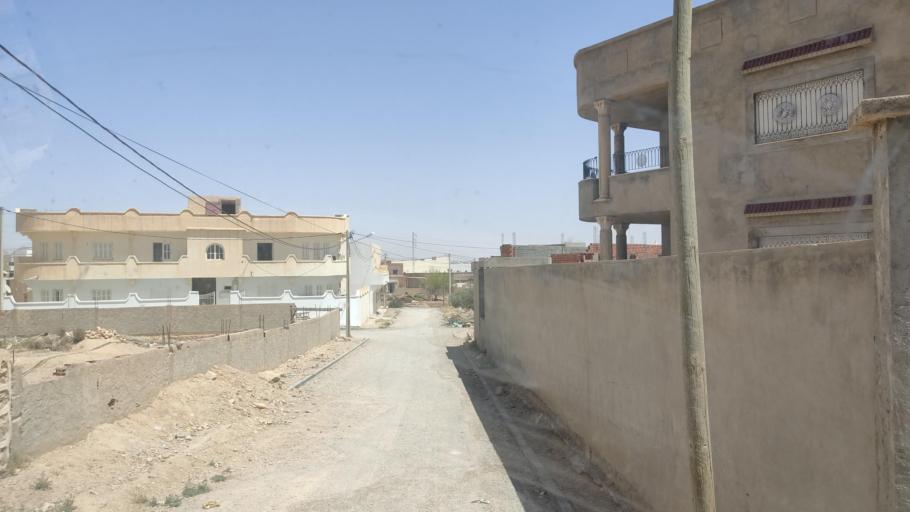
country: TN
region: Gafsa
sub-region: Gafsa Municipality
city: Gafsa
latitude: 34.3399
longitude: 8.9409
